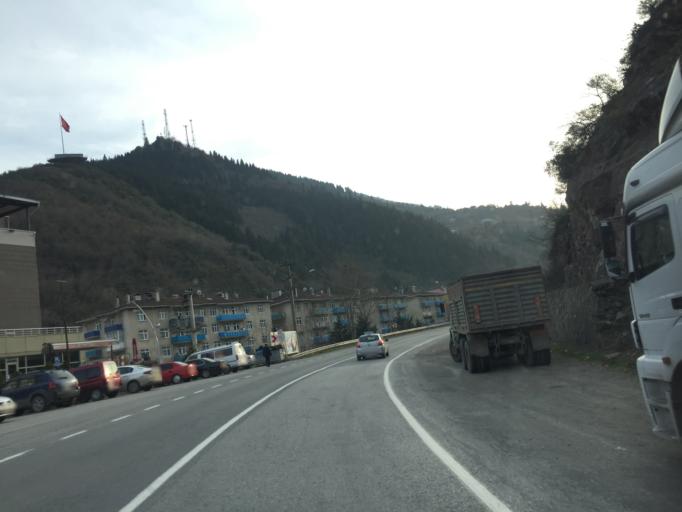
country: TR
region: Trabzon
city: Macka
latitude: 40.8122
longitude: 39.6107
